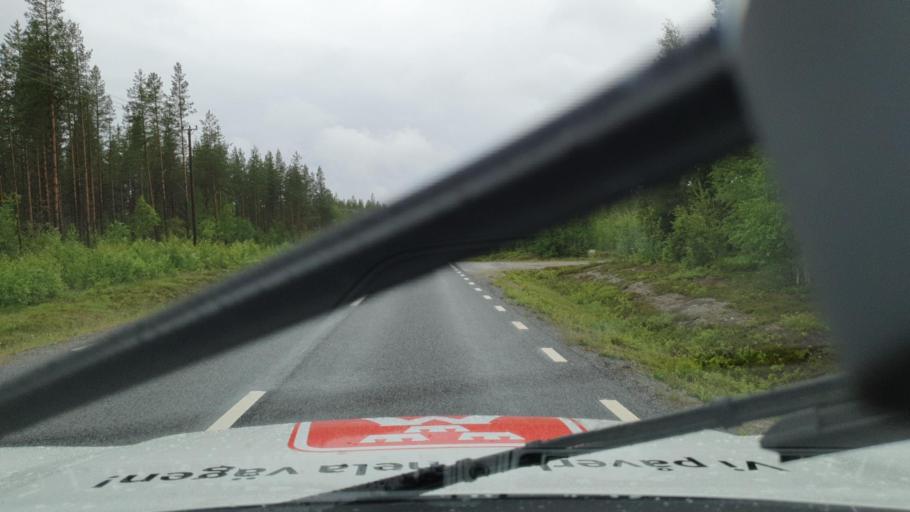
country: SE
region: Vaesterbotten
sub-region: Asele Kommun
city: Asele
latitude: 63.9279
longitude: 17.2623
